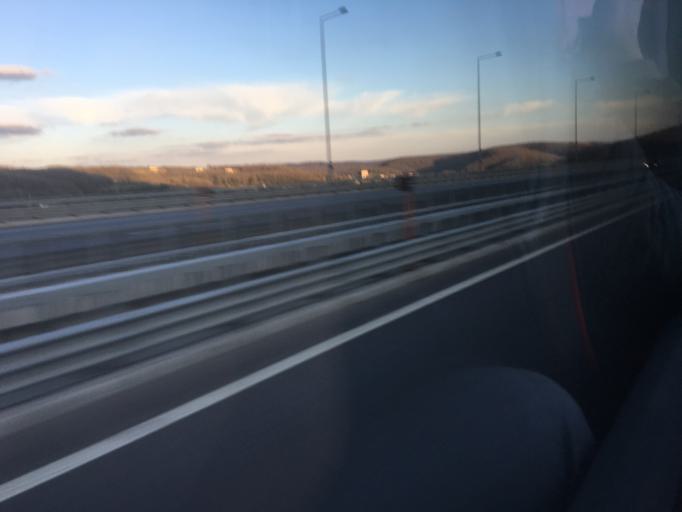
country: TR
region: Istanbul
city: Mahmut Sevket Pasa
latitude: 41.1414
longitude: 29.2838
